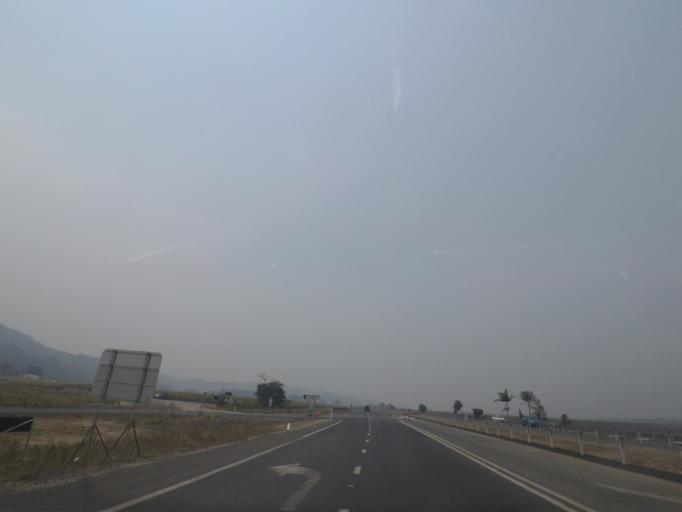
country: AU
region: New South Wales
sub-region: Ballina
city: Ballina
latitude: -28.9017
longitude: 153.4798
